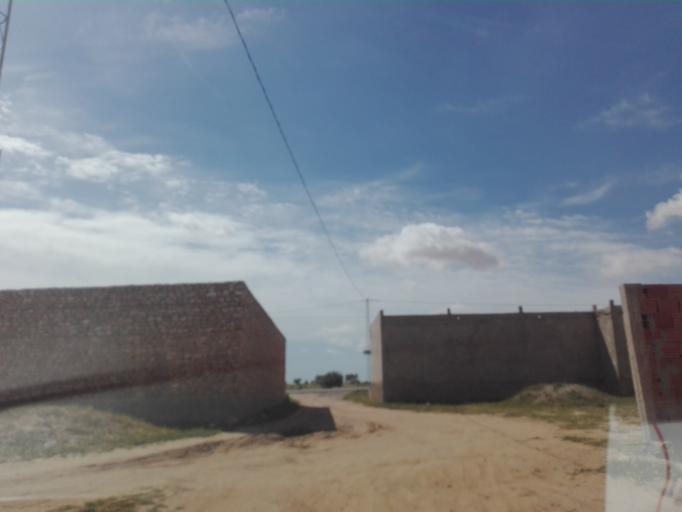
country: TN
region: Safaqis
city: Sfax
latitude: 34.7298
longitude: 10.5062
